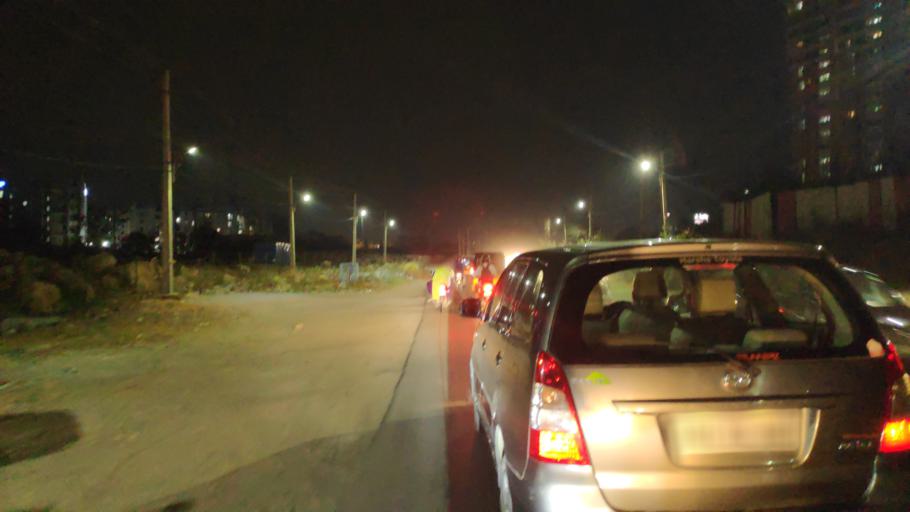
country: IN
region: Telangana
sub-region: Rangareddi
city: Kukatpalli
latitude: 17.4764
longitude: 78.3796
